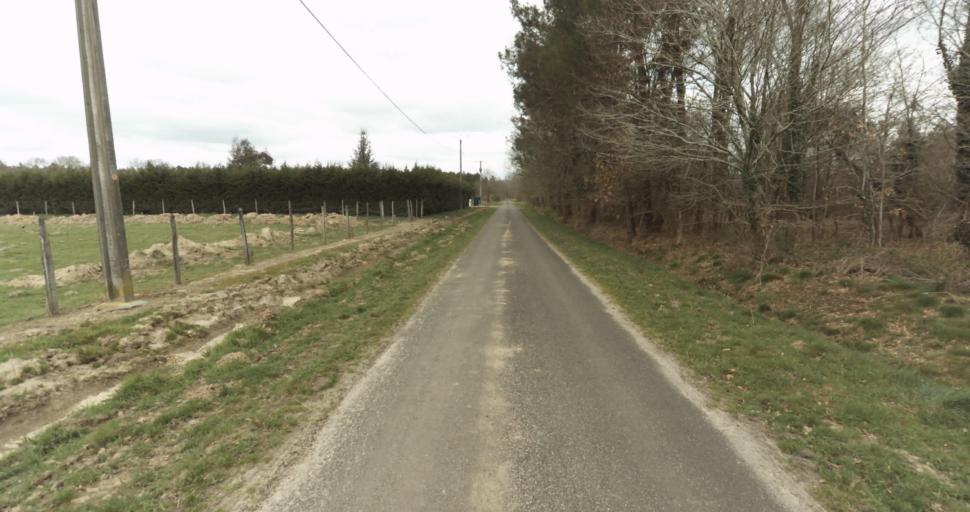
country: FR
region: Aquitaine
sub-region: Departement des Landes
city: Roquefort
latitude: 44.0702
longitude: -0.3830
